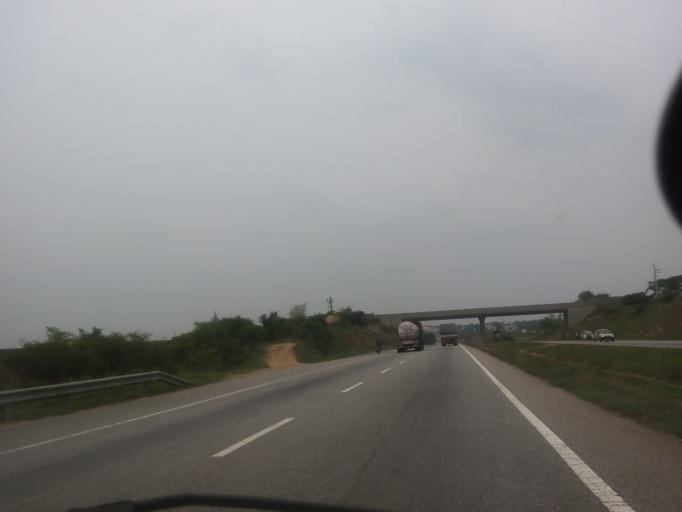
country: IN
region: Karnataka
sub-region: Bangalore Urban
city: Bangalore
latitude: 12.9698
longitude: 77.4713
